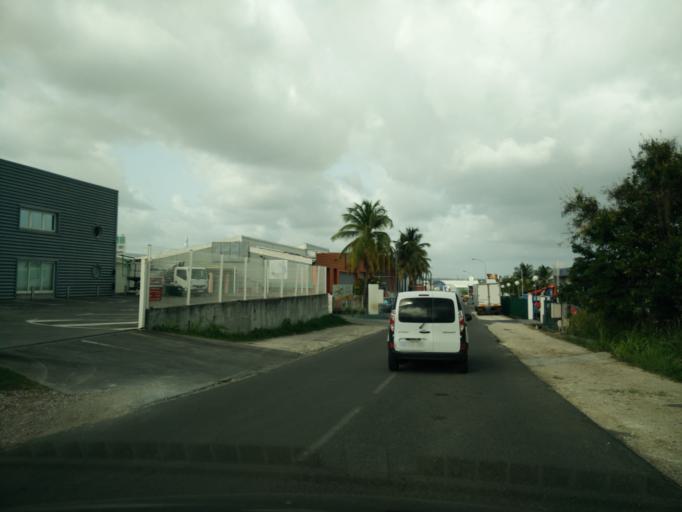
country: GP
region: Guadeloupe
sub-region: Guadeloupe
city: Baie-Mahault
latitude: 16.2385
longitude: -61.5692
